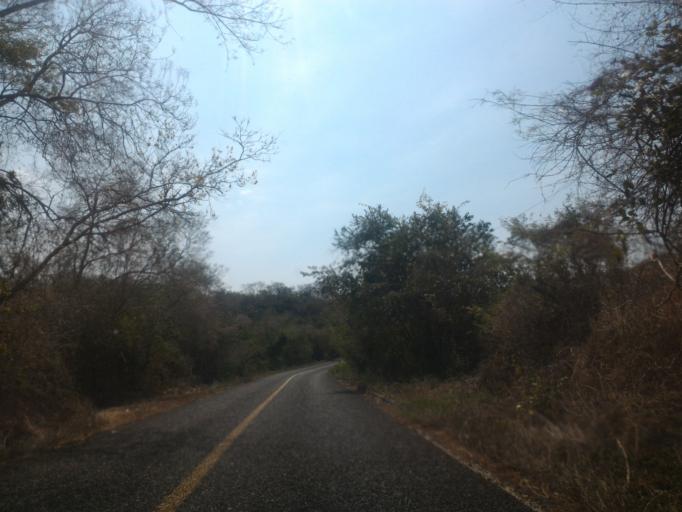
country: MX
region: Michoacan
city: Coahuayana Viejo
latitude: 18.3767
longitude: -103.5137
